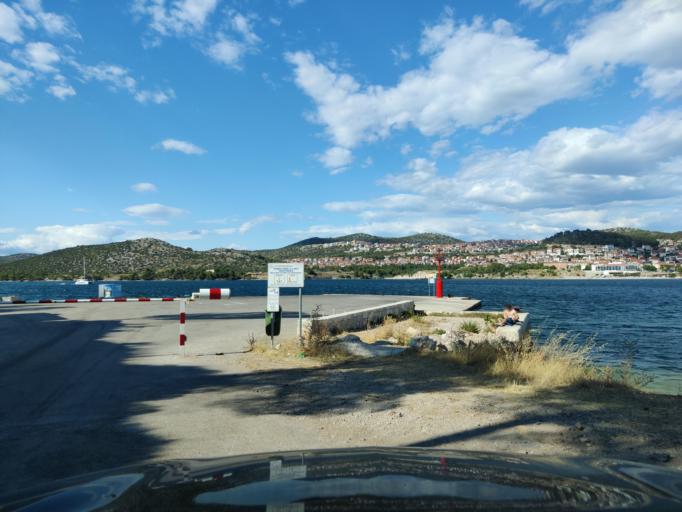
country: HR
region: Sibensko-Kniniska
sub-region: Grad Sibenik
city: Sibenik
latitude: 43.7379
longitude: 15.8757
